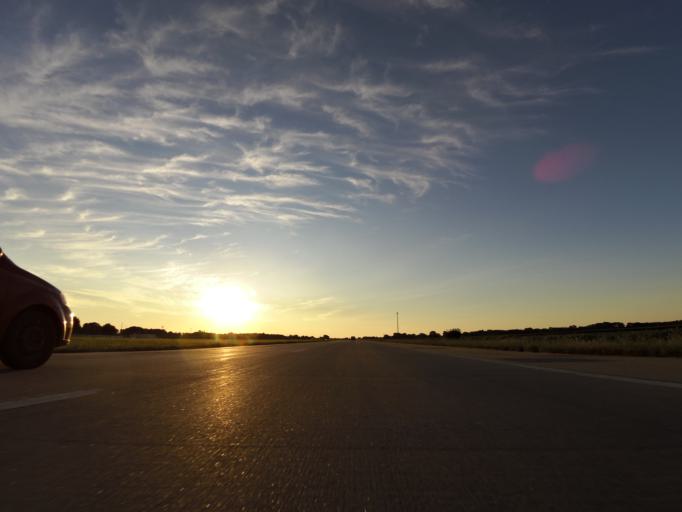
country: US
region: Kansas
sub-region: Reno County
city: Haven
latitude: 37.8955
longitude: -97.7830
